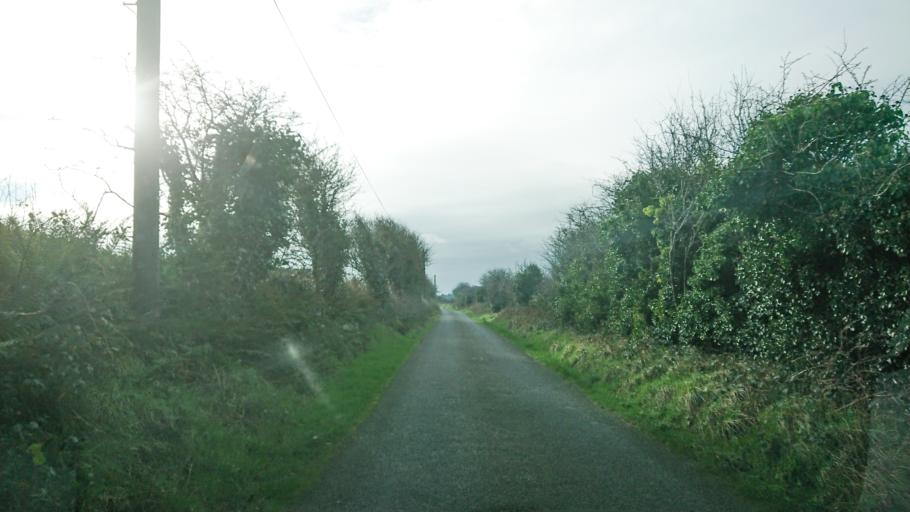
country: IE
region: Munster
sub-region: Waterford
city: Tra Mhor
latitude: 52.1529
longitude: -7.1916
